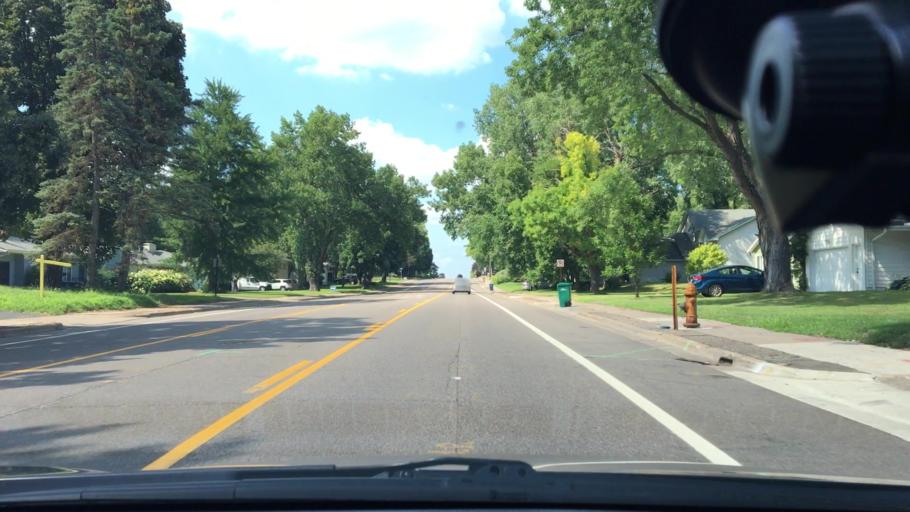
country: US
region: Minnesota
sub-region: Hennepin County
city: Golden Valley
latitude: 44.9981
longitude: -93.3803
